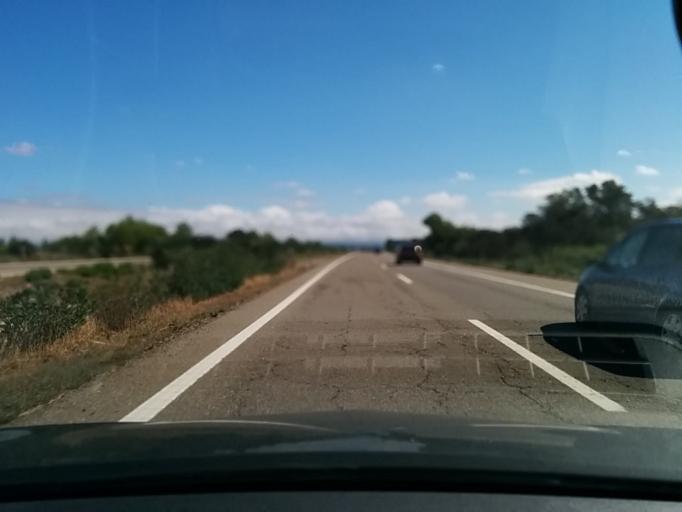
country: ES
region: Aragon
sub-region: Provincia de Huesca
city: Huesca
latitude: 42.1062
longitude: -0.4570
